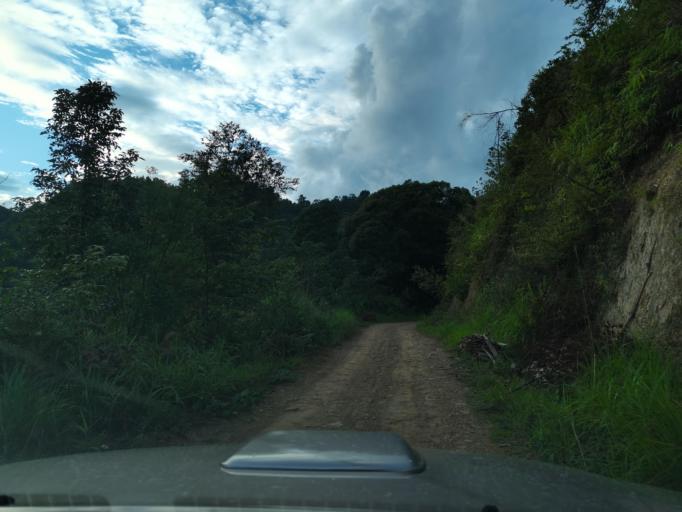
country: LA
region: Phongsali
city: Phongsali
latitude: 21.6513
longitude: 102.1478
